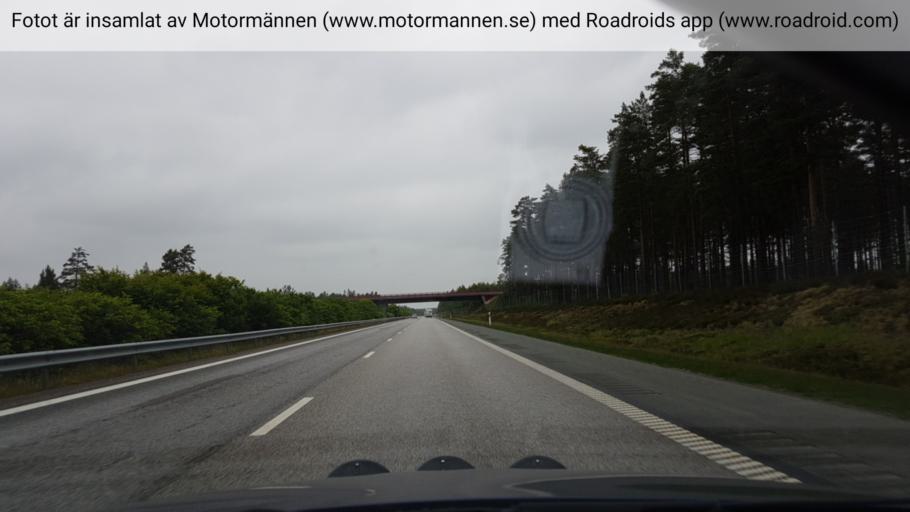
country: SE
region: Joenkoeping
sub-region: Varnamo Kommun
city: Varnamo
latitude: 57.2643
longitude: 14.0831
